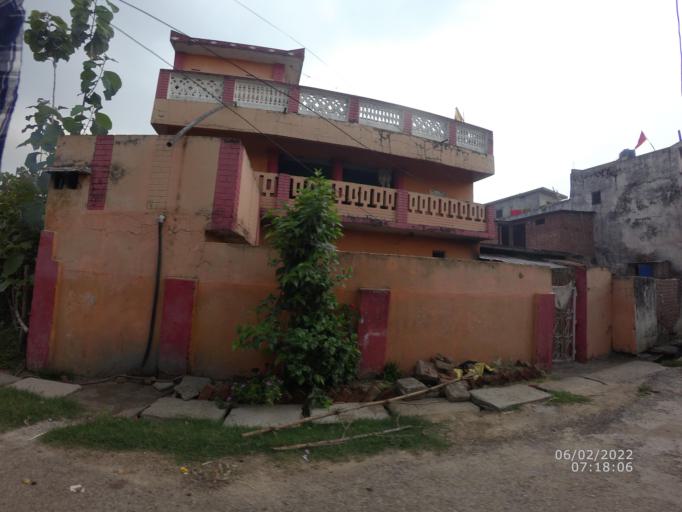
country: NP
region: Western Region
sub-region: Lumbini Zone
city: Bhairahawa
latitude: 27.4844
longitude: 83.4368
